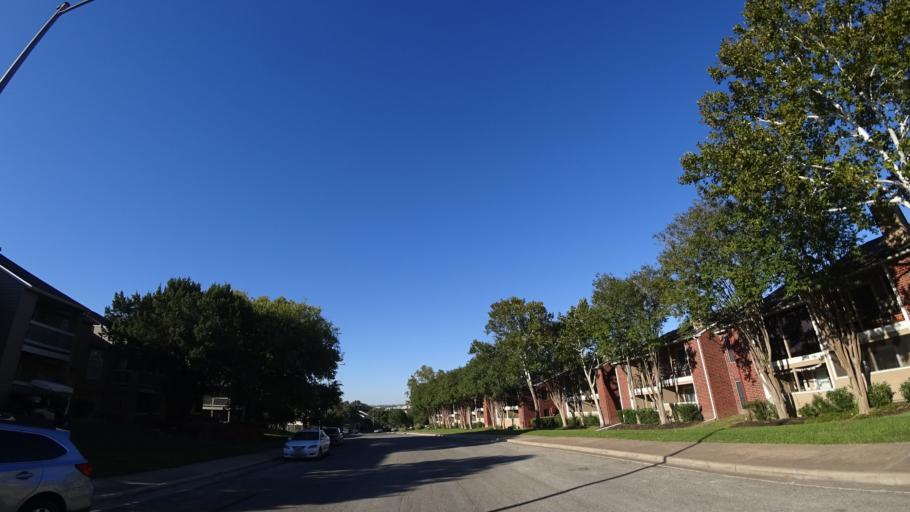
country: US
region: Texas
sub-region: Travis County
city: Austin
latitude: 30.2269
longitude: -97.7191
